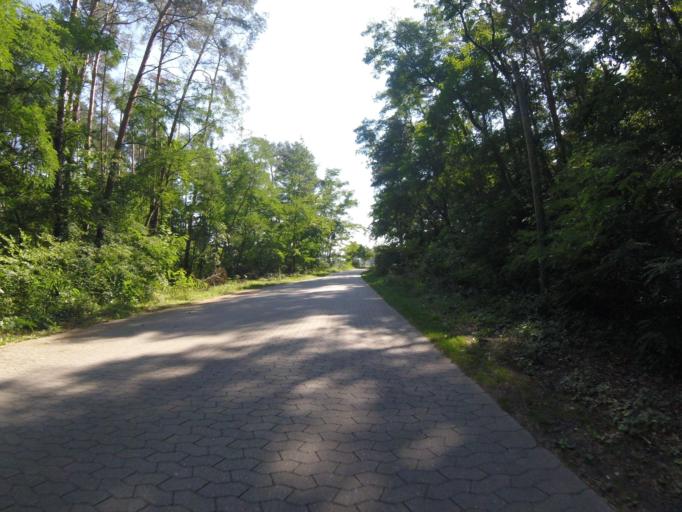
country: DE
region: Brandenburg
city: Bestensee
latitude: 52.2480
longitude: 13.6995
